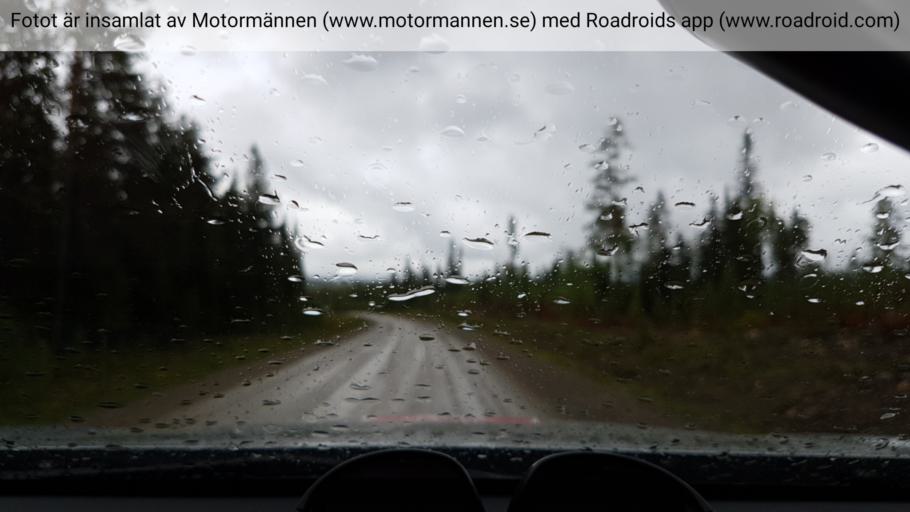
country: SE
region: Vaesterbotten
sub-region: Asele Kommun
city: Insjon
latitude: 64.8293
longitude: 17.4648
